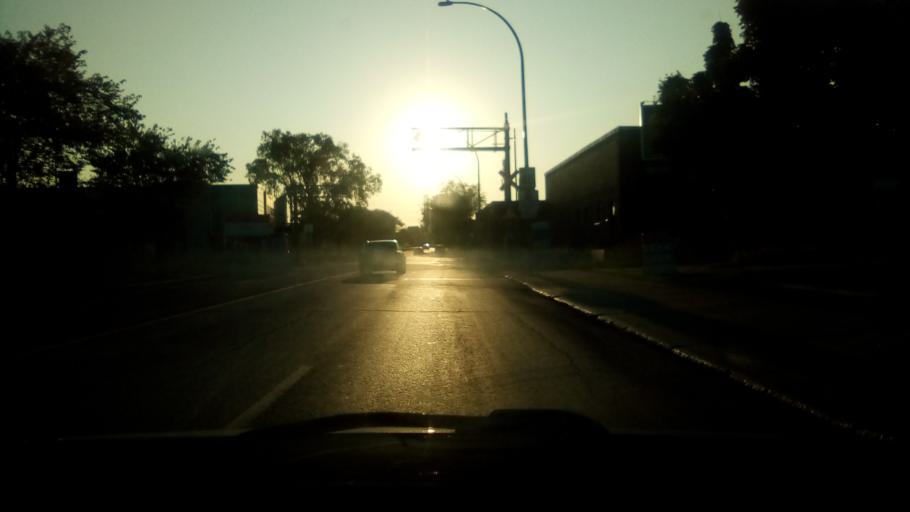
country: CA
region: Quebec
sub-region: Montreal
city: Montreal
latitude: 45.4867
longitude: -73.5508
